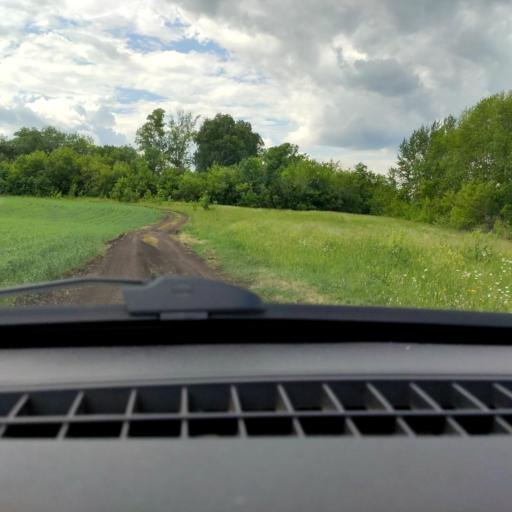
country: RU
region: Bashkortostan
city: Kabakovo
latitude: 54.5179
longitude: 56.0888
